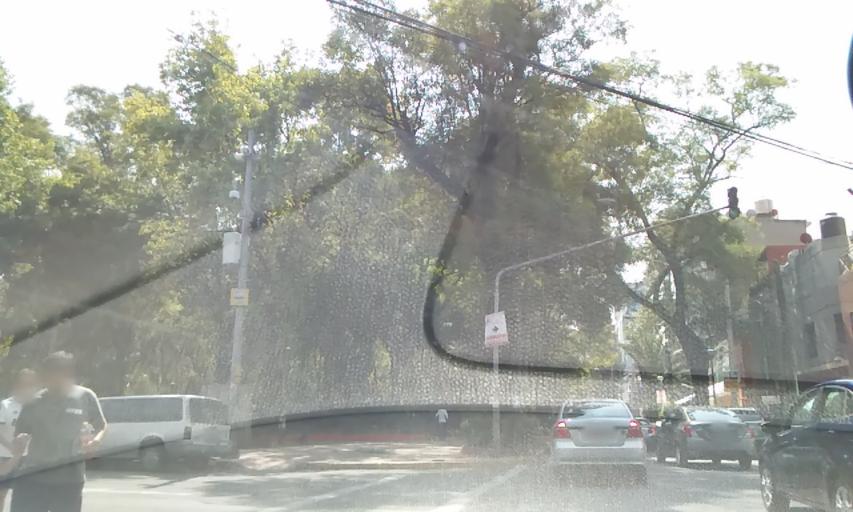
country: MX
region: Mexico City
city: Cuauhtemoc
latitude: 19.4328
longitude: -99.1632
